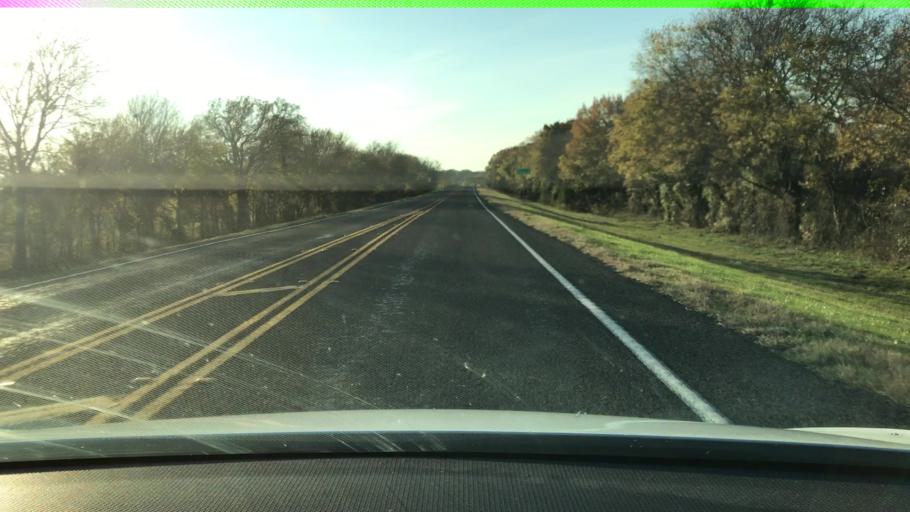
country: US
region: Texas
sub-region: Kaufman County
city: Kemp
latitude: 32.5701
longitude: -96.1311
